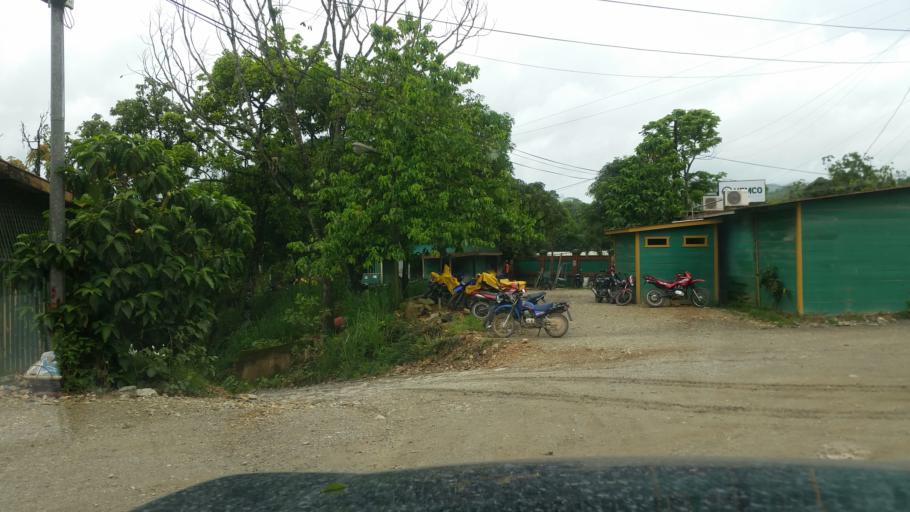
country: NI
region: Atlantico Norte (RAAN)
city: Bonanza
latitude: 14.0312
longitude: -84.5949
